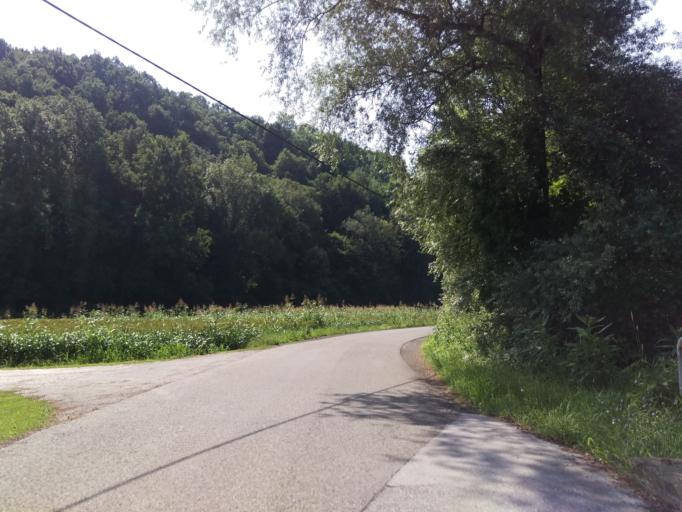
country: AT
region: Styria
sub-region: Politischer Bezirk Graz-Umgebung
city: Werndorf
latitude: 46.9080
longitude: 15.4936
